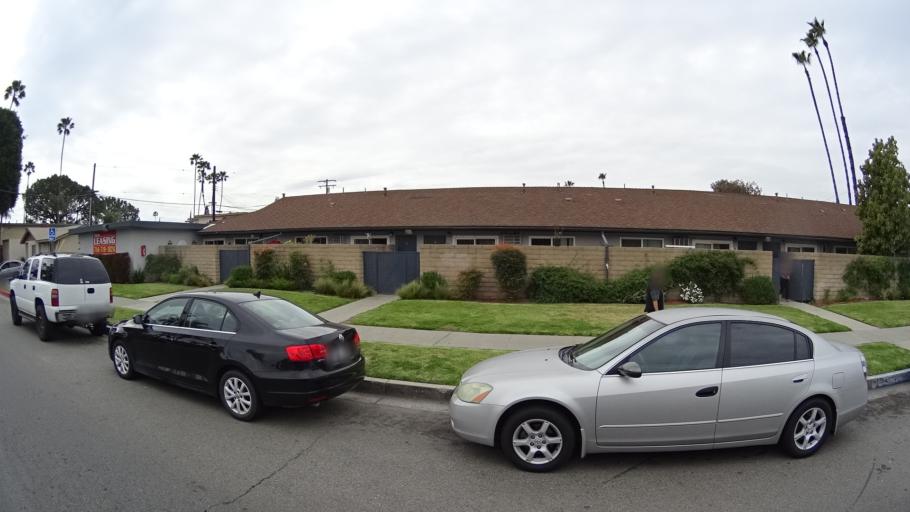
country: US
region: California
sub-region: Orange County
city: Anaheim
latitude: 33.8438
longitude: -117.9373
